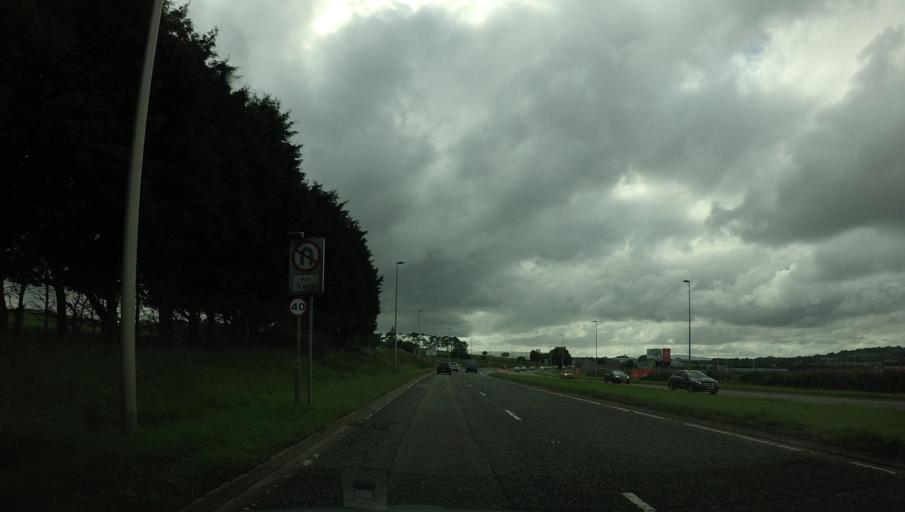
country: GB
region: Scotland
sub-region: Aberdeenshire
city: Westhill
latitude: 57.1474
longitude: -2.2497
